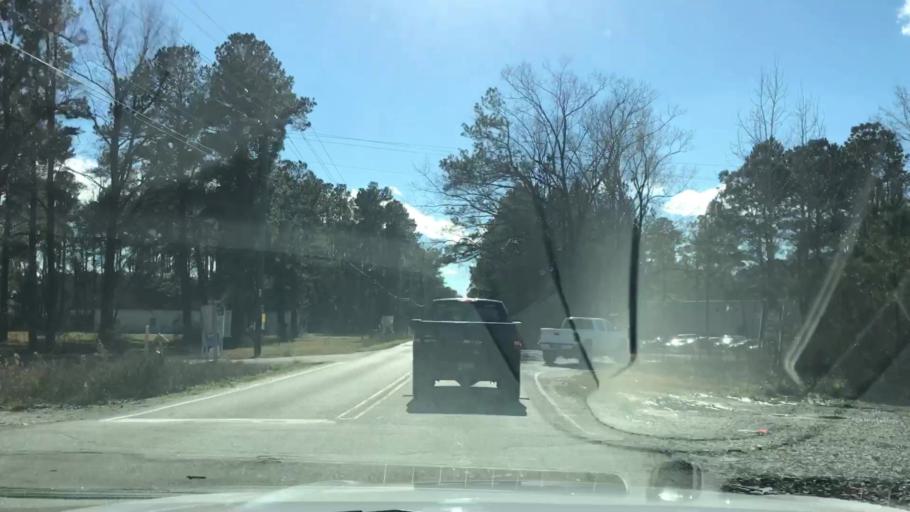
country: US
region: South Carolina
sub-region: Dorchester County
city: Summerville
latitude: 33.0549
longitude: -80.2392
